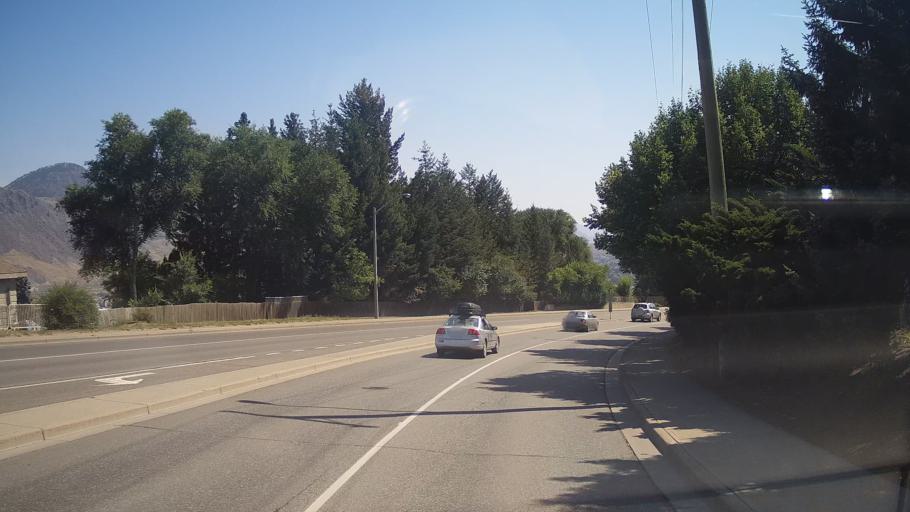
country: CA
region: British Columbia
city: Kamloops
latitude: 50.6739
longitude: -120.3493
